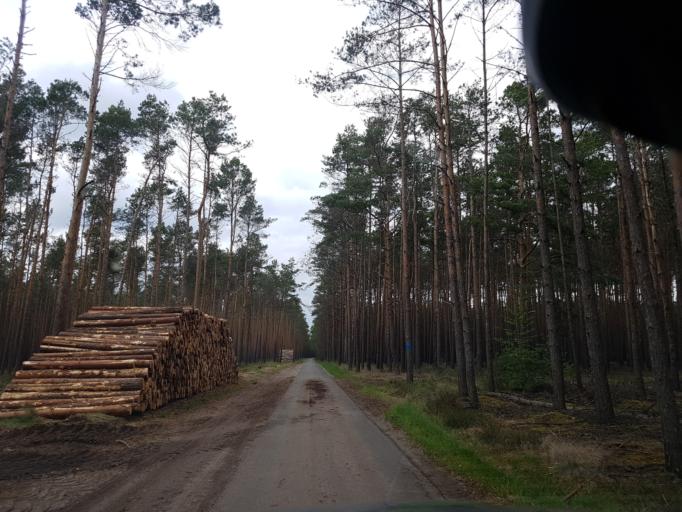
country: DE
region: Brandenburg
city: Crinitz
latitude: 51.6777
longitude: 13.7805
